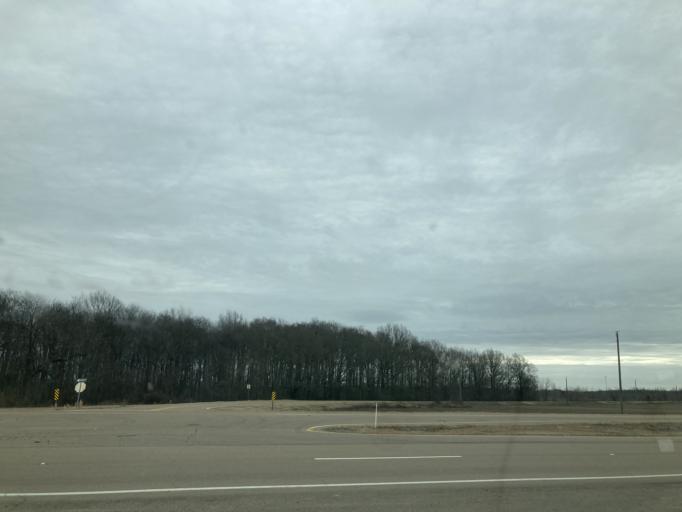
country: US
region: Mississippi
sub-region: Yazoo County
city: Yazoo City
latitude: 33.0041
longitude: -90.4704
